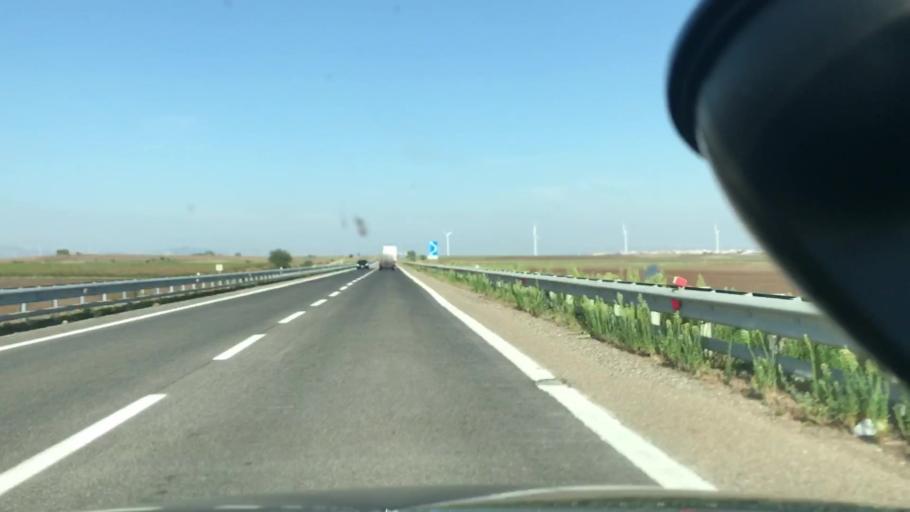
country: IT
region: Basilicate
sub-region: Provincia di Potenza
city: Venosa
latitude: 41.0108
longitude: 15.8355
